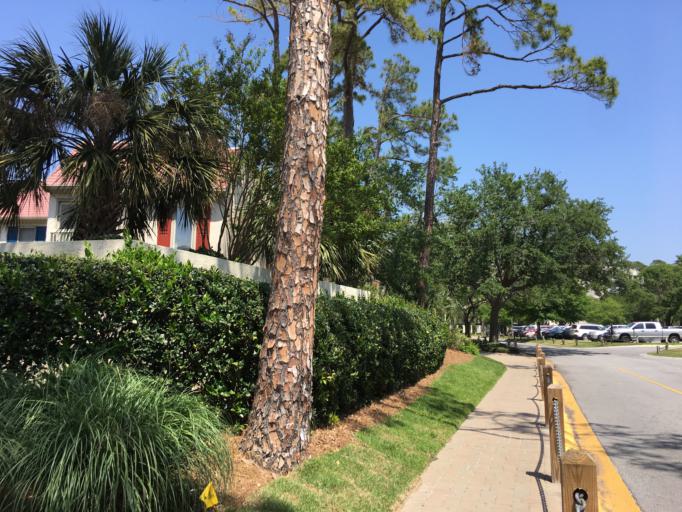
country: US
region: South Carolina
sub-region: Beaufort County
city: Hilton Head Island
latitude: 32.1394
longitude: -80.8118
